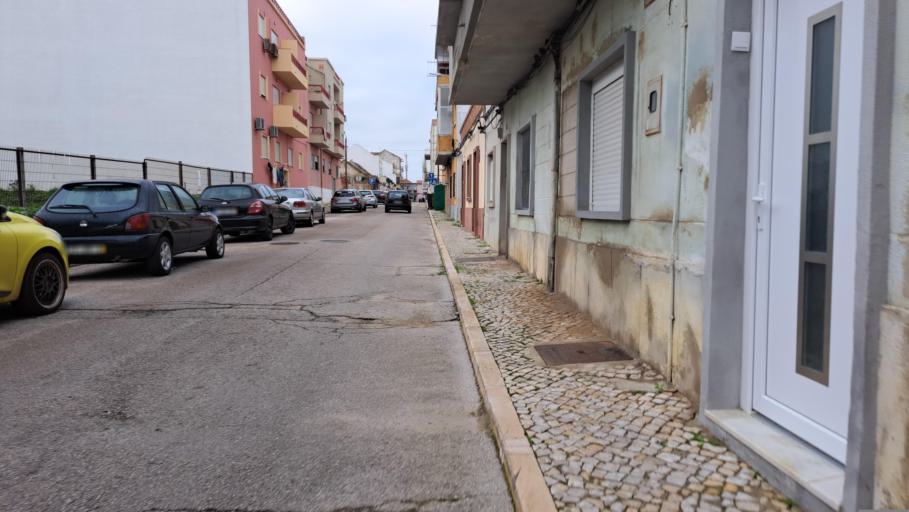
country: PT
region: Setubal
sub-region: Moita
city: Alhos Vedros
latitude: 38.6587
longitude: -9.0470
